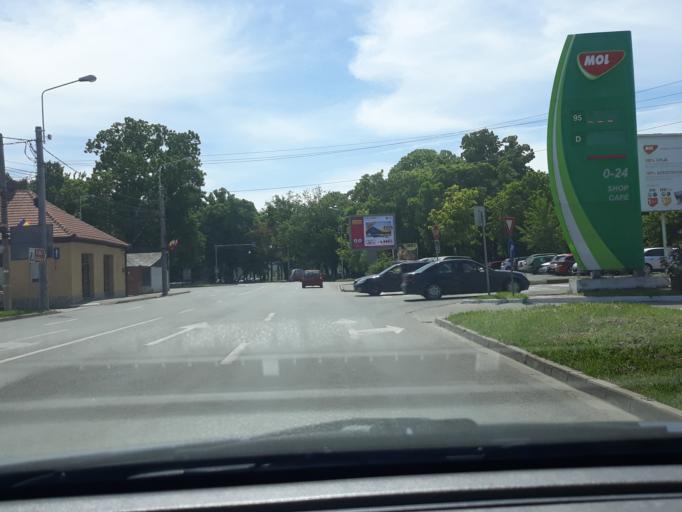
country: RO
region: Bihor
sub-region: Comuna Biharea
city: Oradea
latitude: 47.0517
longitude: 21.9193
